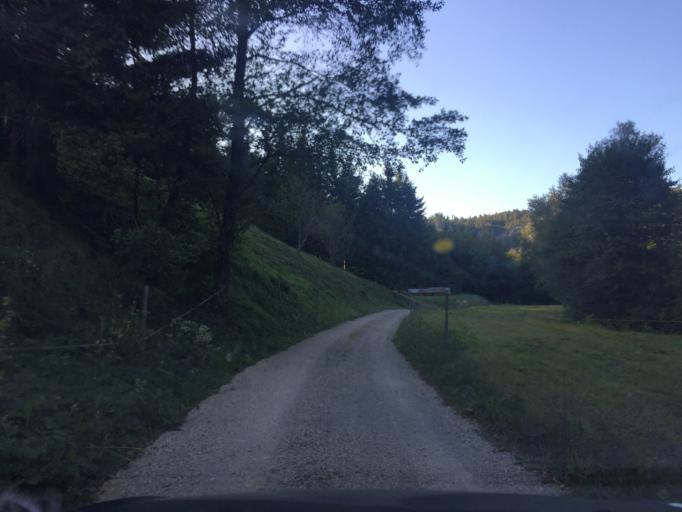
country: SI
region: Postojna
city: Postojna
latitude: 45.8100
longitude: 14.1328
